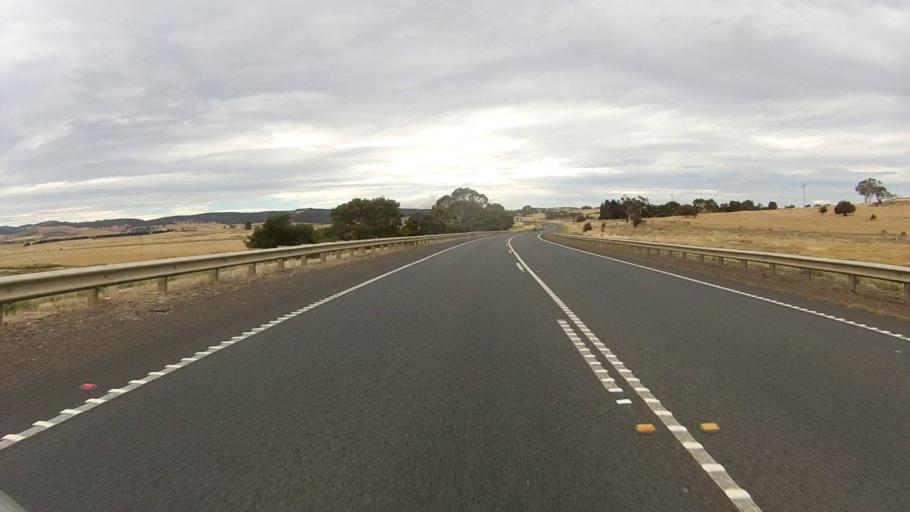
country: AU
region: Tasmania
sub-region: Brighton
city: Bridgewater
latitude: -42.3217
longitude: 147.3461
